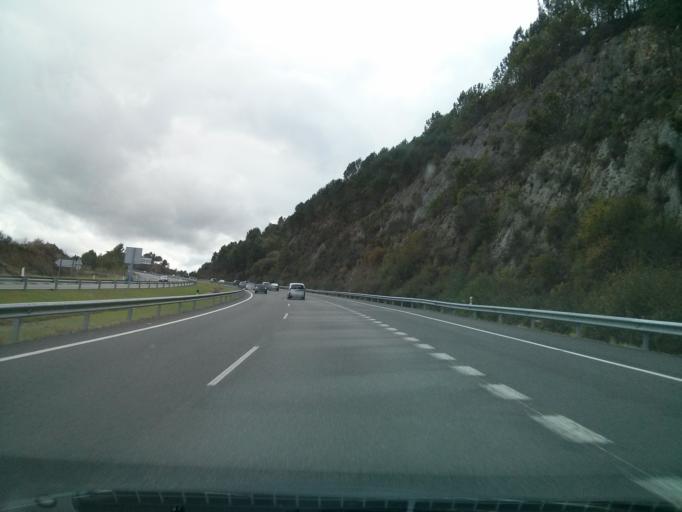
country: ES
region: Galicia
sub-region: Provincia de Ourense
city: Punxin
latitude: 42.3417
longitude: -8.0136
